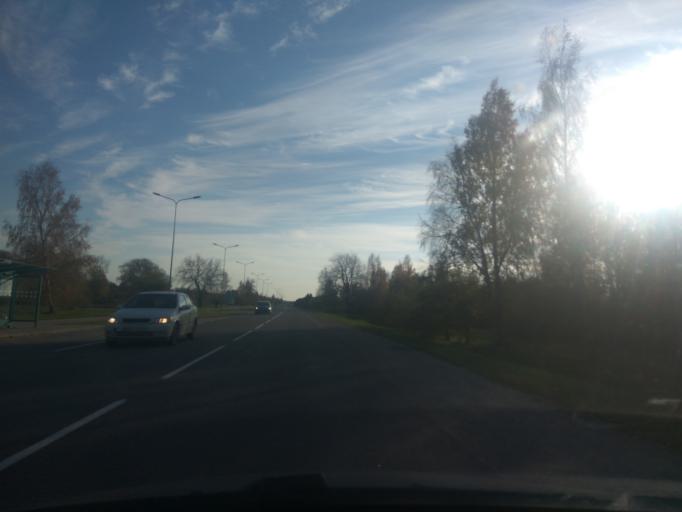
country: LV
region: Ventspils
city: Ventspils
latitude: 57.3606
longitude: 21.5631
